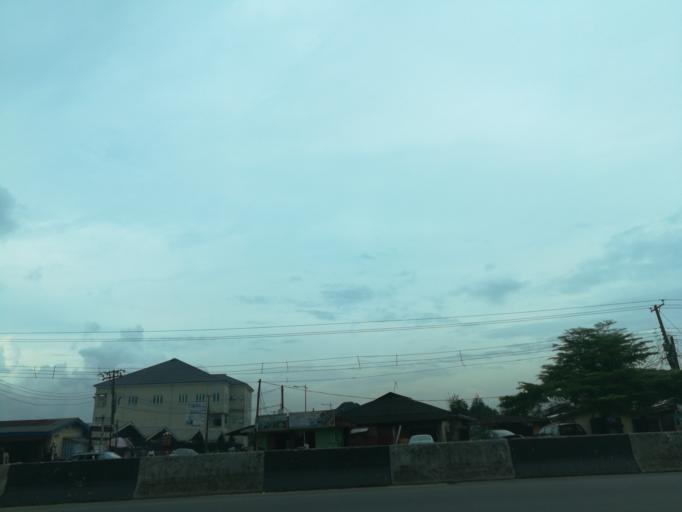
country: NG
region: Rivers
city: Port Harcourt
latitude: 4.8128
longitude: 7.0101
